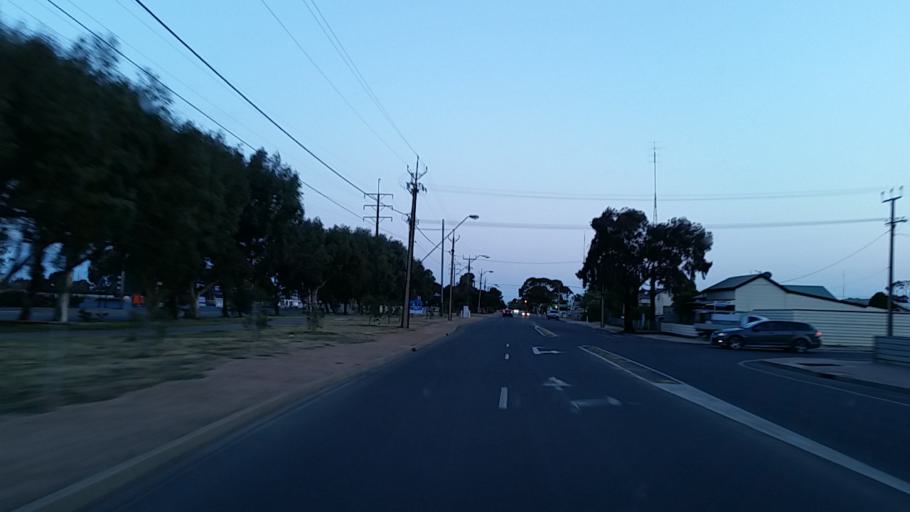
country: AU
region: South Australia
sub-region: Port Pirie City and Dists
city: Port Pirie
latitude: -33.1849
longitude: 138.0039
